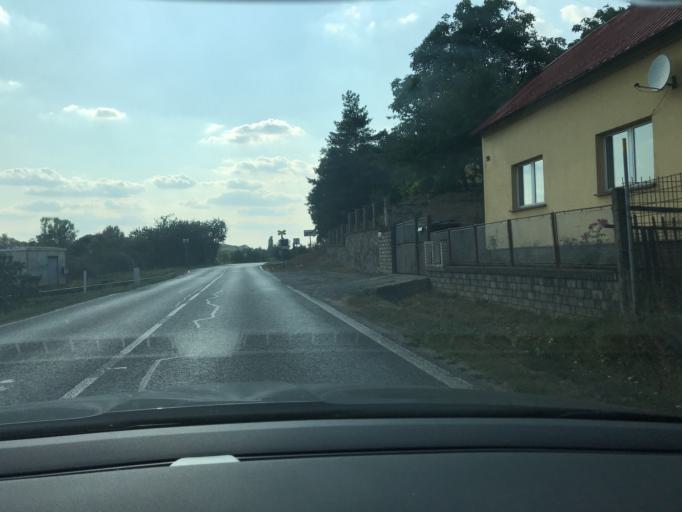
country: CZ
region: Central Bohemia
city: Kralupy nad Vltavou
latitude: 50.2326
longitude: 14.2778
